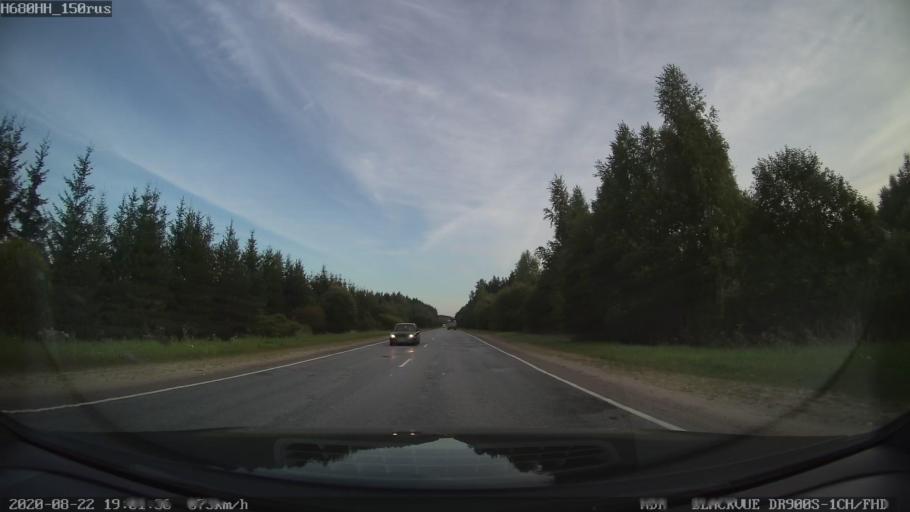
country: RU
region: Tverskaya
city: Vasil'yevskiy Mokh
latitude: 57.1175
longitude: 36.1158
